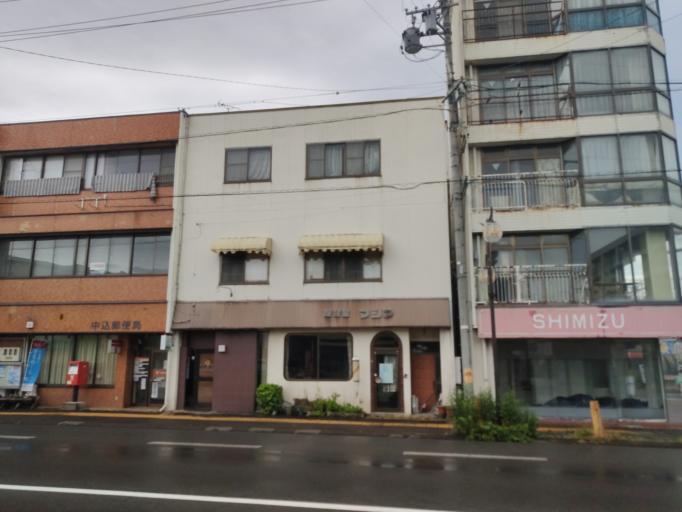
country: JP
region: Nagano
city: Saku
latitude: 36.2294
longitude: 138.4769
